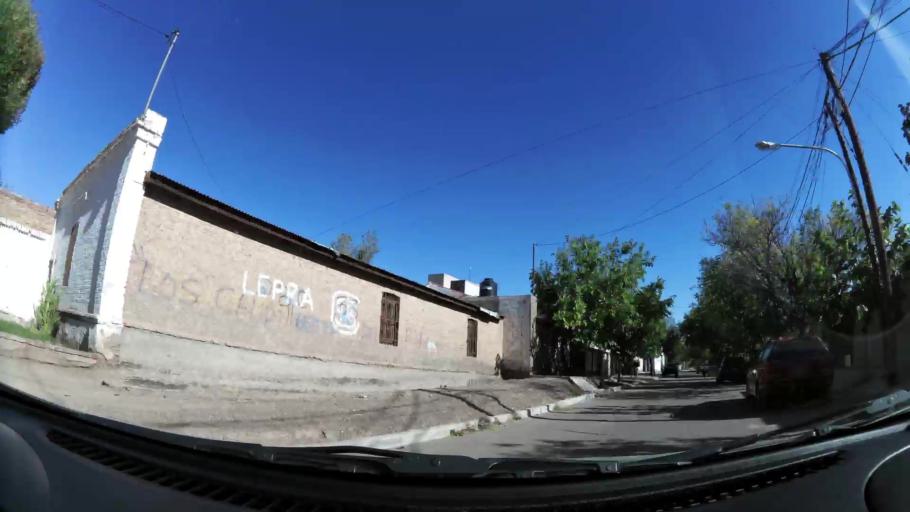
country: AR
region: Mendoza
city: Mendoza
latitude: -32.9028
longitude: -68.8152
